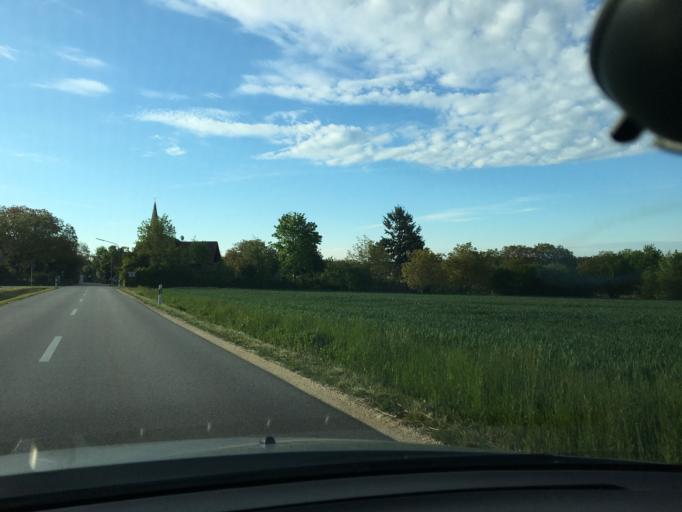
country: DE
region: Bavaria
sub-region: Lower Bavaria
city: Stallwang
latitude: 48.5161
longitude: 12.2189
